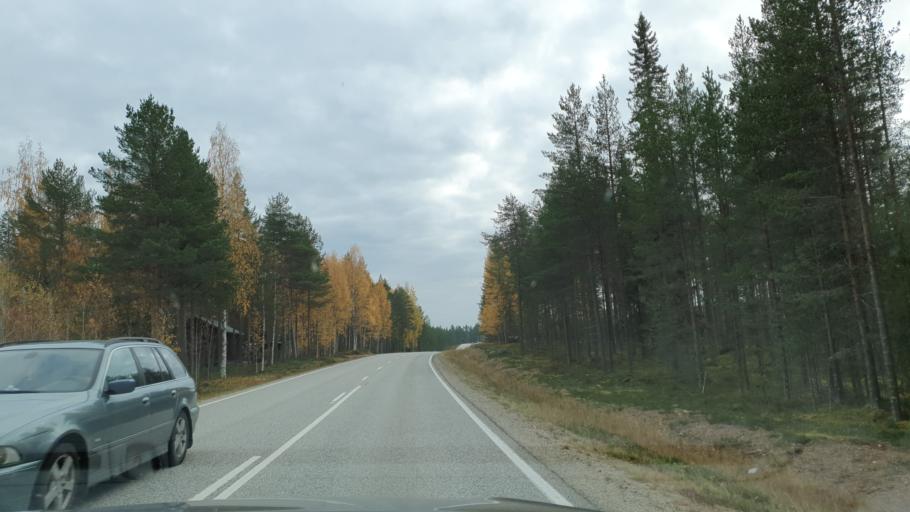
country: FI
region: Kainuu
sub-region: Kehys-Kainuu
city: Puolanka
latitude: 65.2377
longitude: 27.5883
